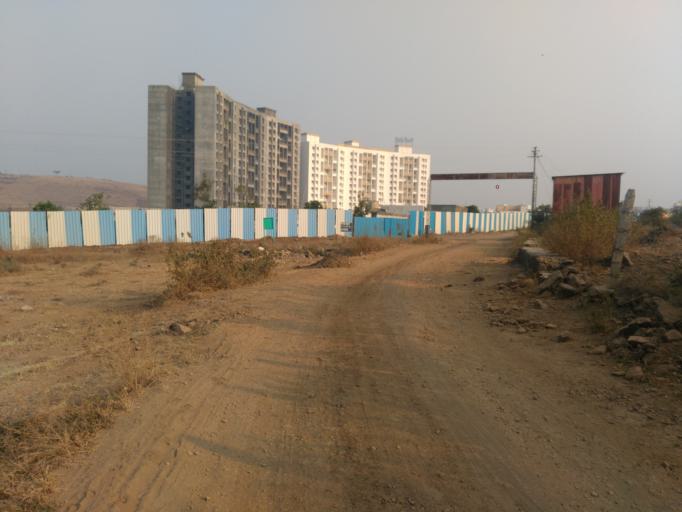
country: IN
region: Maharashtra
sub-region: Pune Division
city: Pune
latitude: 18.4317
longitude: 73.8873
